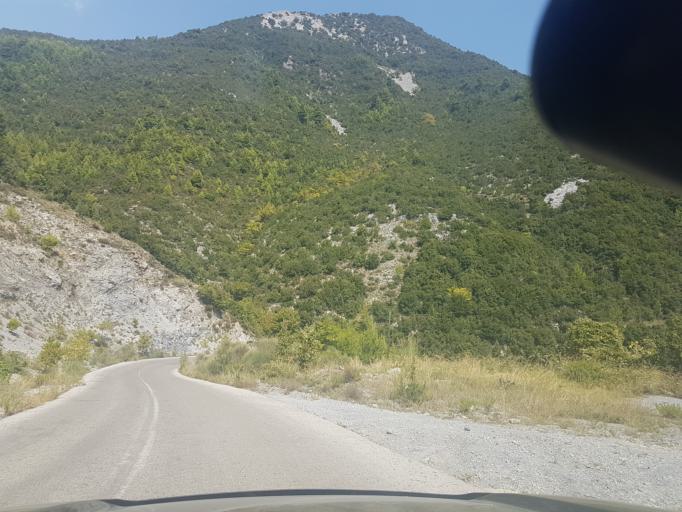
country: GR
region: Central Greece
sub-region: Nomos Evvoias
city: Kymi
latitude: 38.6495
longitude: 23.9026
